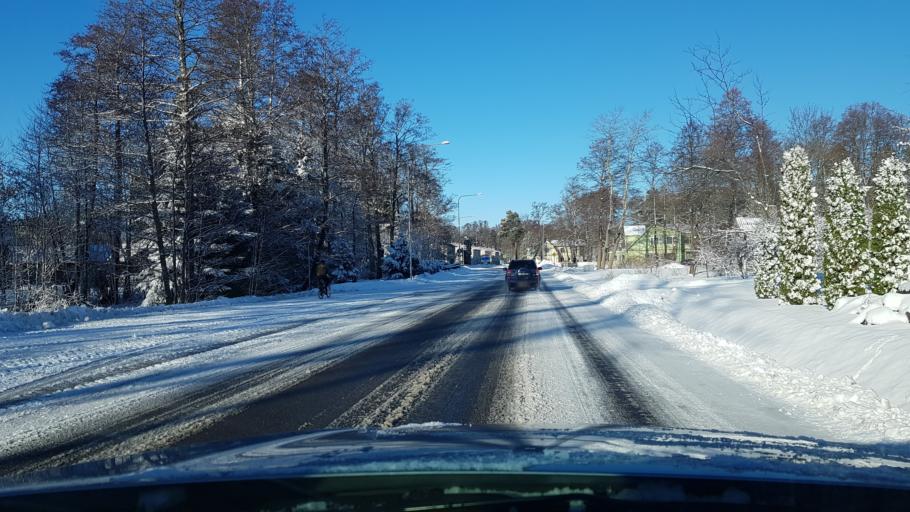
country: EE
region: Hiiumaa
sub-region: Kaerdla linn
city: Kardla
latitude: 58.9924
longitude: 22.7475
